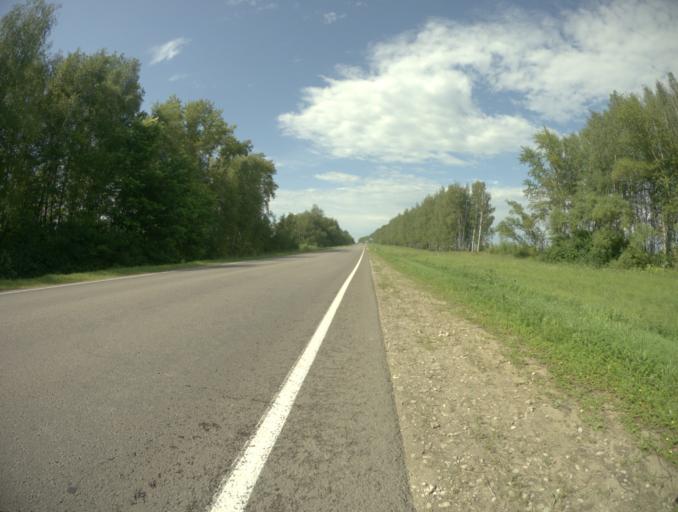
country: RU
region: Vladimir
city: Suzdal'
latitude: 56.3916
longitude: 40.4518
